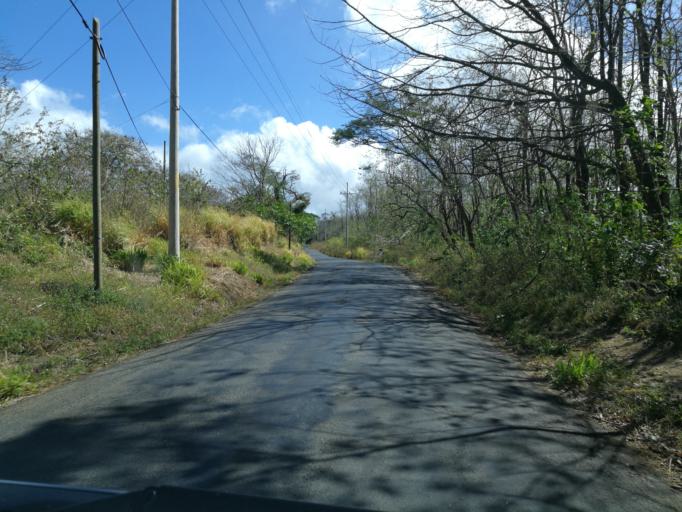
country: CR
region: Guanacaste
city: Liberia
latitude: 10.7272
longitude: -85.3947
